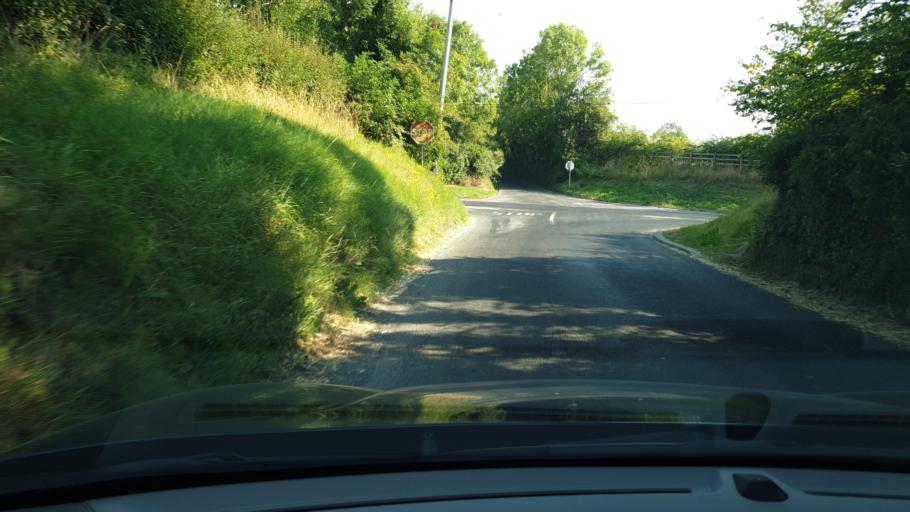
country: IE
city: Kentstown
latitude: 53.5962
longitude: -6.4900
